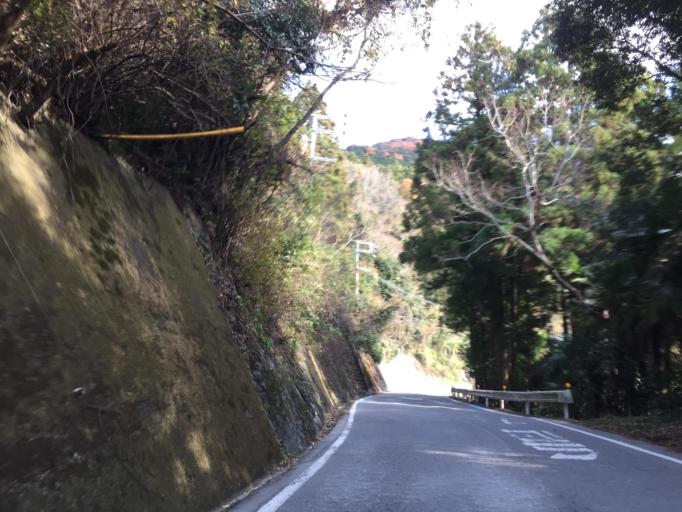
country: JP
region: Wakayama
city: Iwade
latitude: 34.1496
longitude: 135.3731
